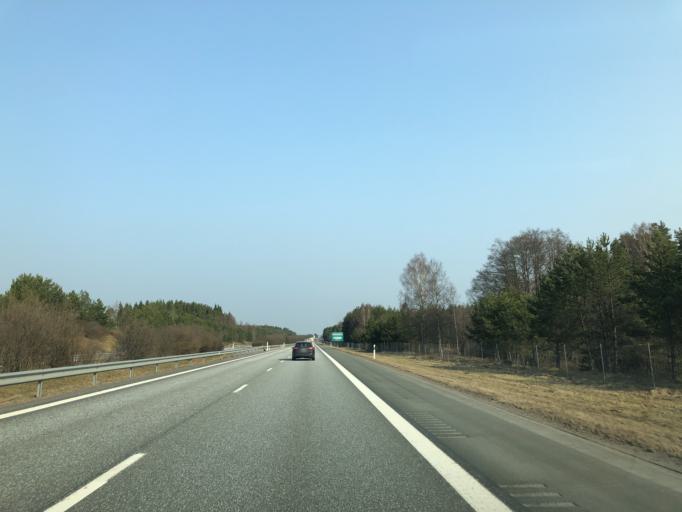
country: SE
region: Joenkoeping
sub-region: Vaggeryds Kommun
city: Skillingaryd
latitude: 57.4328
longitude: 14.1035
